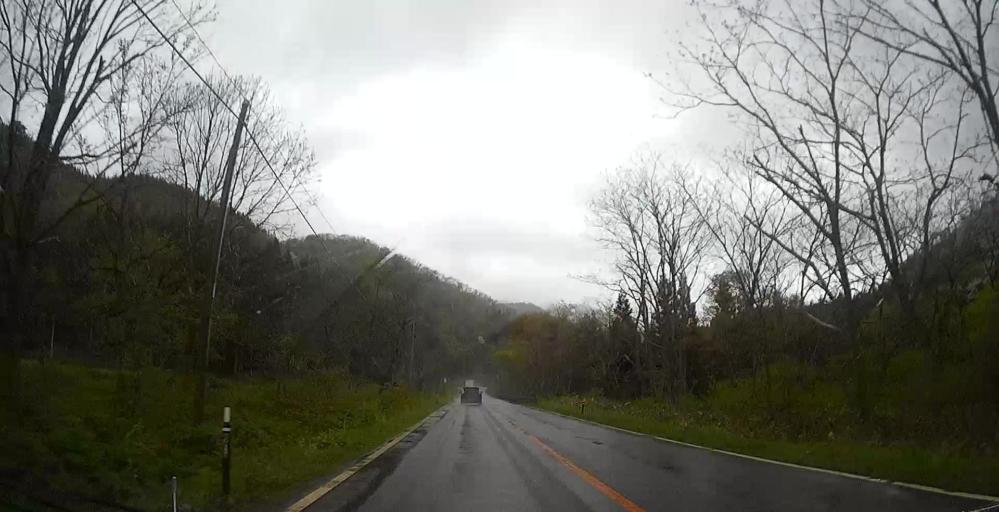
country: JP
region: Yamagata
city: Nagai
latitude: 38.0497
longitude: 139.8251
